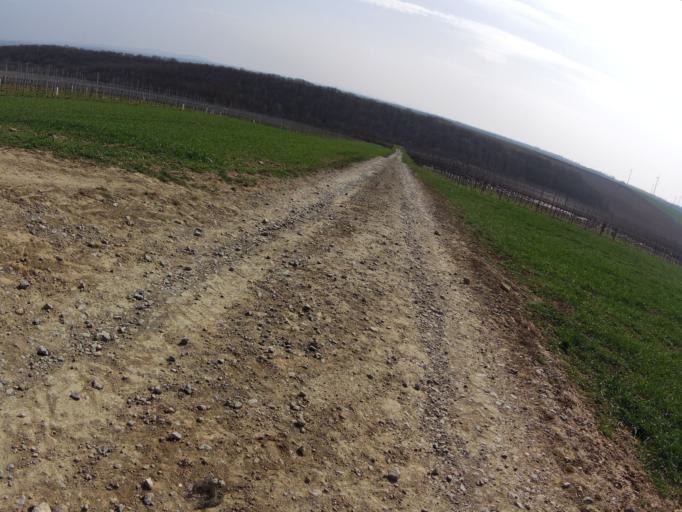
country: DE
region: Bavaria
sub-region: Regierungsbezirk Unterfranken
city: Mainstockheim
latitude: 49.7891
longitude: 10.1380
